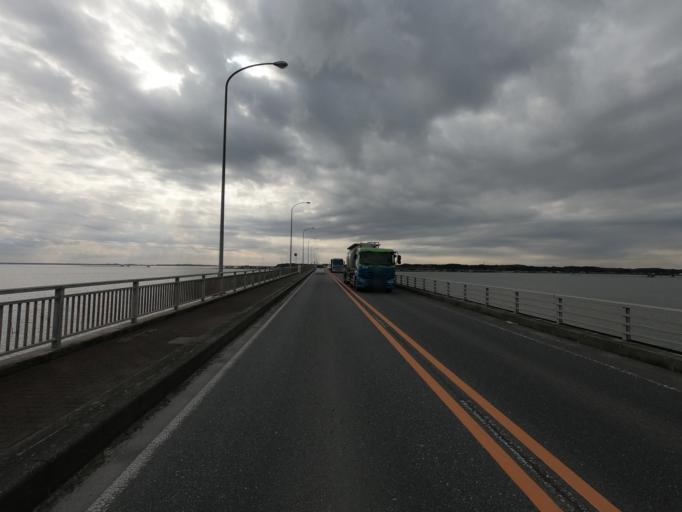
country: JP
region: Ibaraki
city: Inashiki
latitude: 36.0938
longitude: 140.4008
